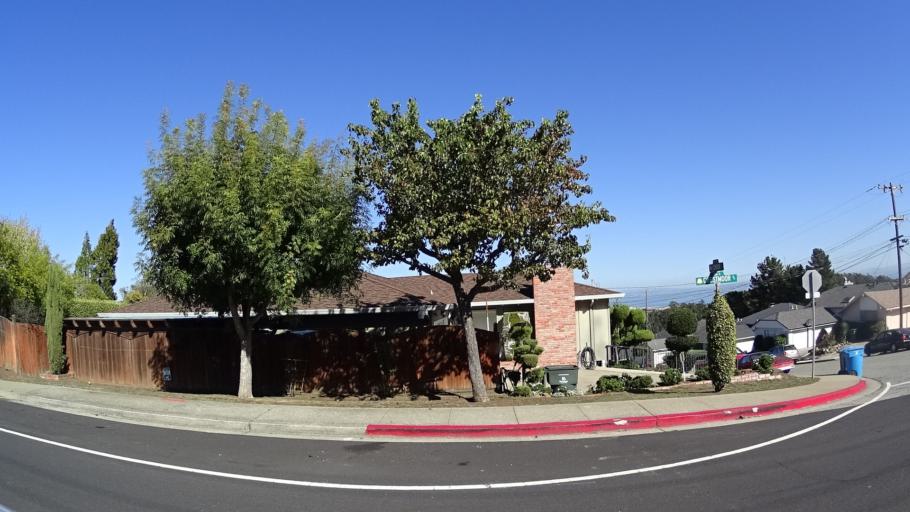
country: US
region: California
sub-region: San Mateo County
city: San Bruno
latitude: 37.6082
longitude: -122.4307
